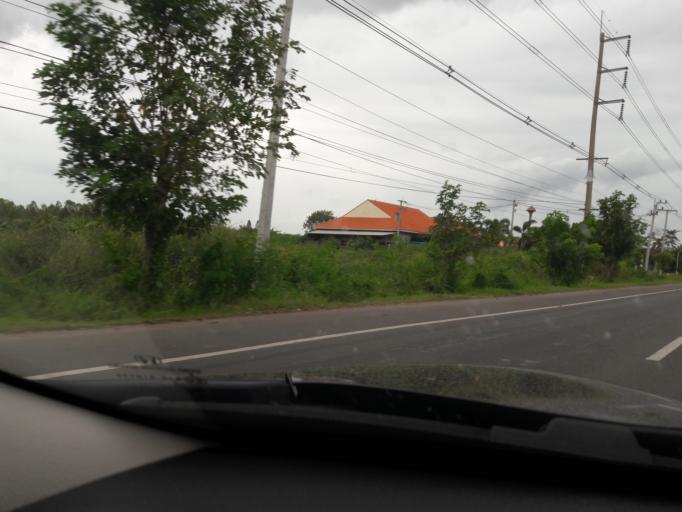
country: TH
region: Ratchaburi
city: Bang Phae
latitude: 13.6406
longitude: 99.9486
